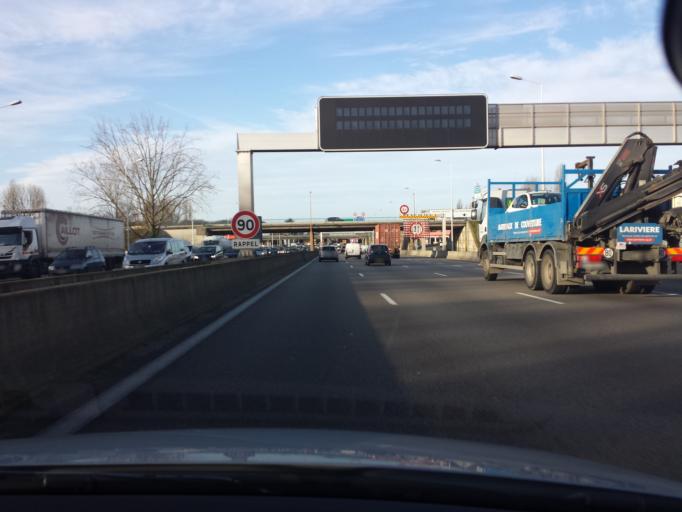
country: FR
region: Ile-de-France
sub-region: Departement des Yvelines
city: Velizy-Villacoublay
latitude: 48.7808
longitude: 2.1759
